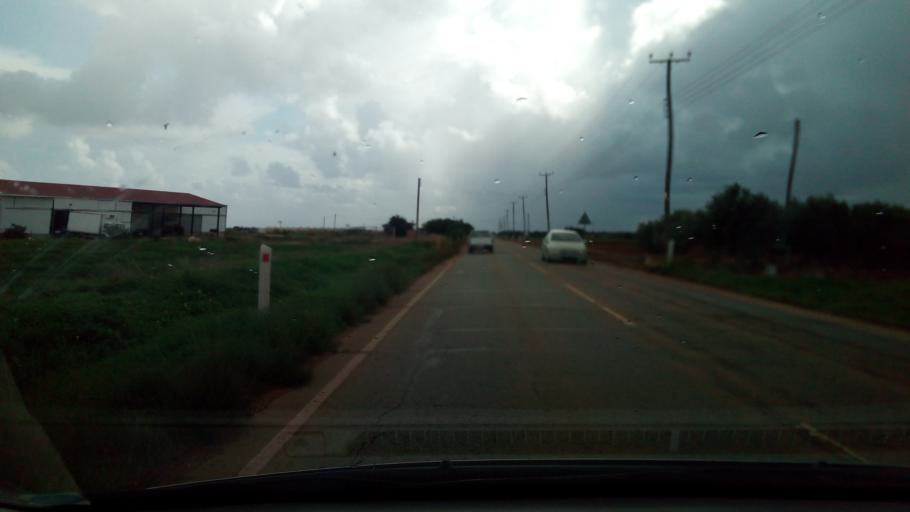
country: CY
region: Ammochostos
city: Liopetri
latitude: 34.9900
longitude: 33.8928
